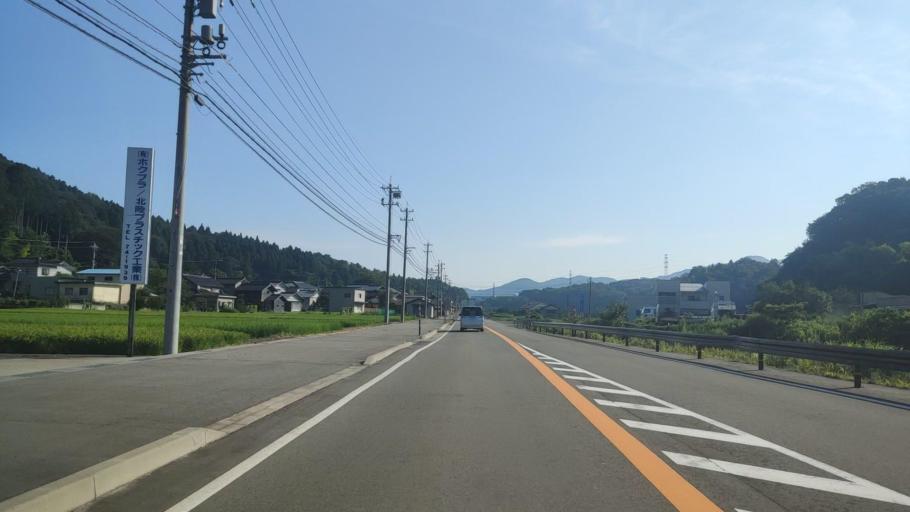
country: JP
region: Fukui
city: Maruoka
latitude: 36.2149
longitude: 136.2726
